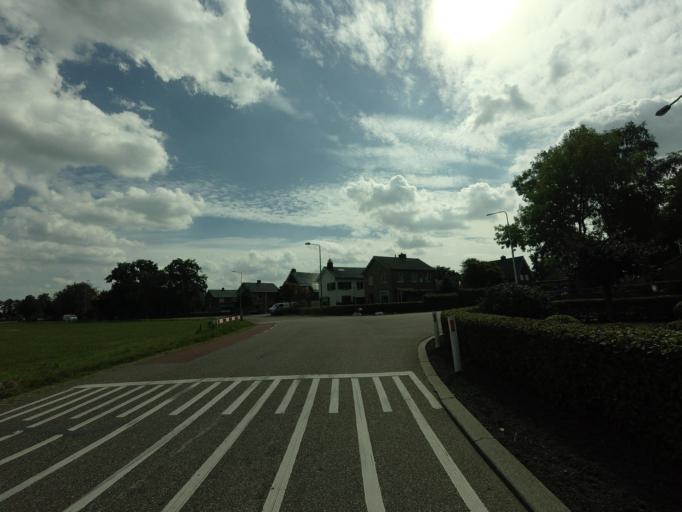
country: NL
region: Gelderland
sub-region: Gemeente Ede
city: Ederveen
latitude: 52.0900
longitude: 5.5756
